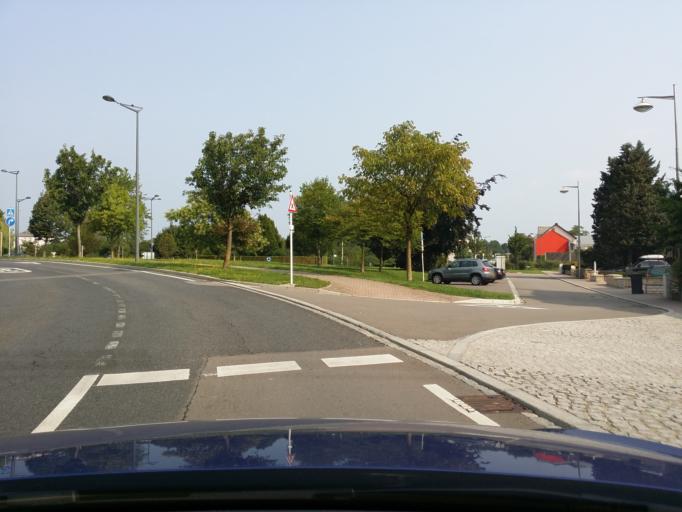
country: LU
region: Luxembourg
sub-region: Canton de Luxembourg
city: Bertrange
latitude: 49.6142
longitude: 6.0608
